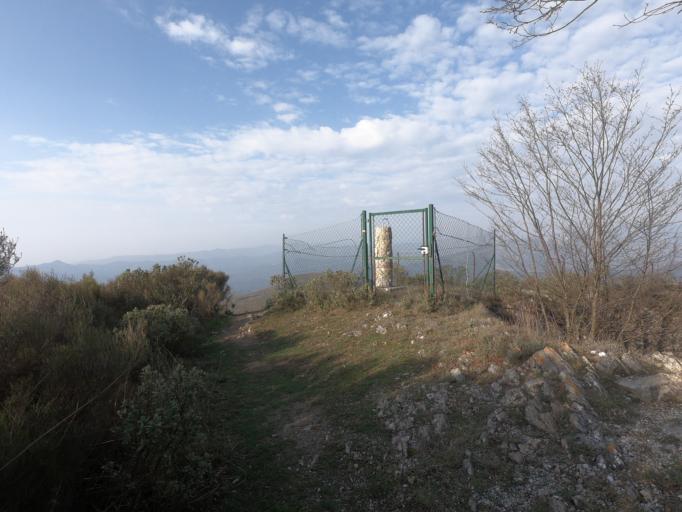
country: IT
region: Liguria
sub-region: Provincia di Savona
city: Balestrino
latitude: 44.1096
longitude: 8.1595
